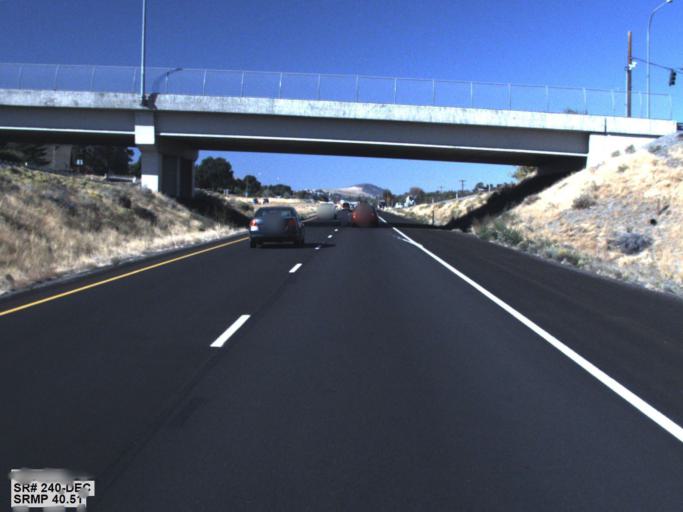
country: US
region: Washington
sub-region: Franklin County
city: West Pasco
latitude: 46.2287
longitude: -119.1904
